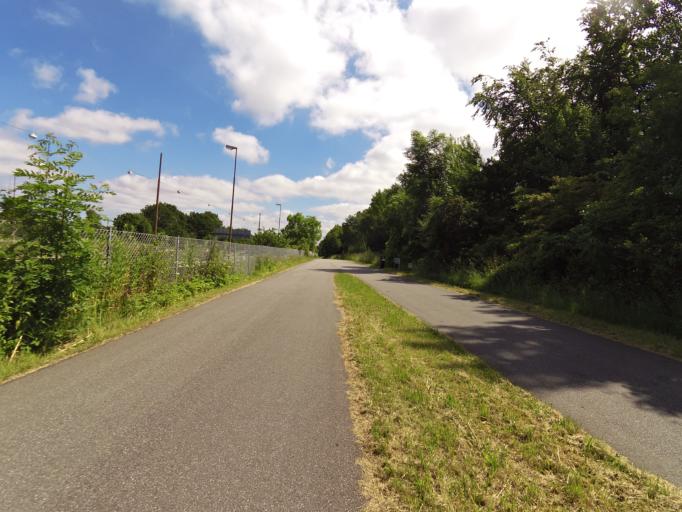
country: DK
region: Capital Region
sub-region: Herlev Kommune
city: Herlev
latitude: 55.7351
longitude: 12.4651
